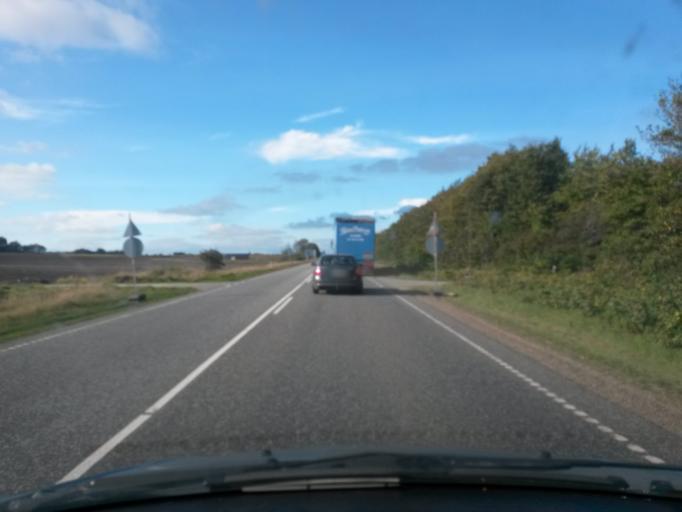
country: DK
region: Central Jutland
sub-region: Herning Kommune
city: Avlum
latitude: 56.2958
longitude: 8.7241
